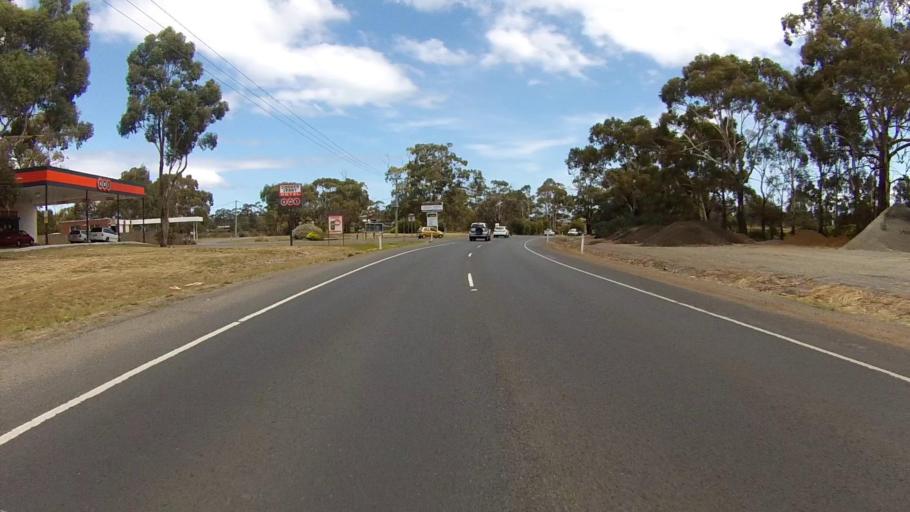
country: AU
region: Tasmania
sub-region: Sorell
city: Sorell
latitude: -42.8488
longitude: 147.6271
